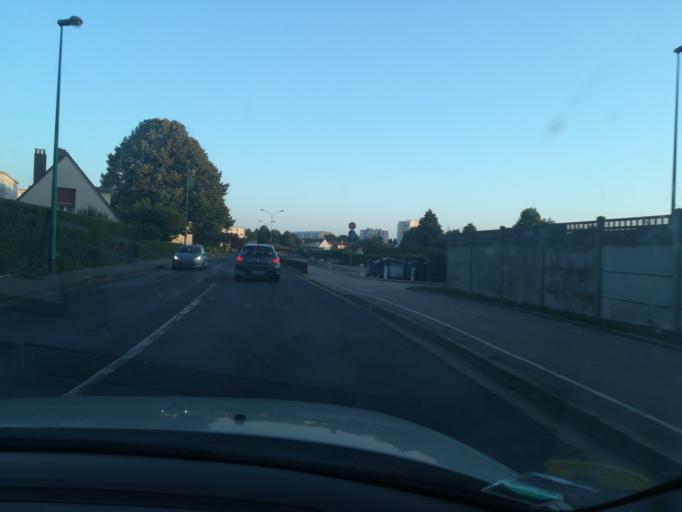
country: FR
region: Haute-Normandie
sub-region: Departement de la Seine-Maritime
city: Bois-Guillaume
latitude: 49.4648
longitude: 1.1295
